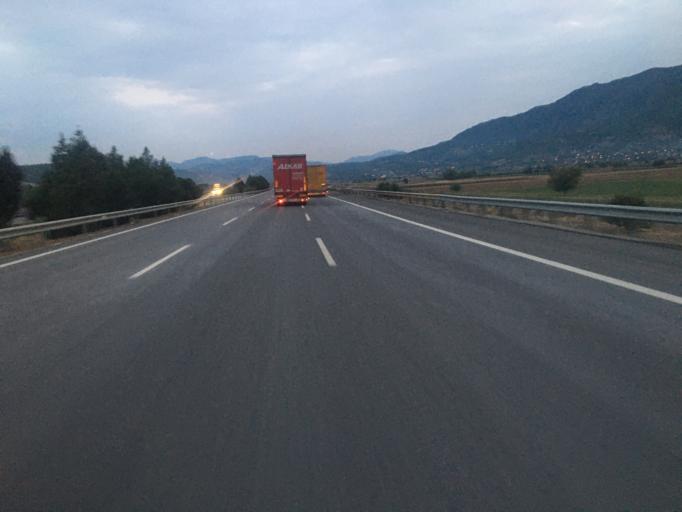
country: TR
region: Osmaniye
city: Osmaniye
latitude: 37.1434
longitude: 36.3269
